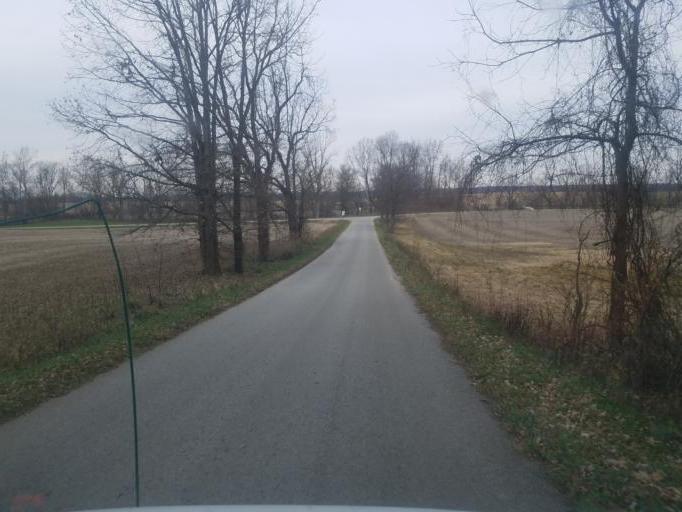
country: US
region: Ohio
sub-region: Knox County
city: Fredericktown
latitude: 40.4531
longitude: -82.6679
